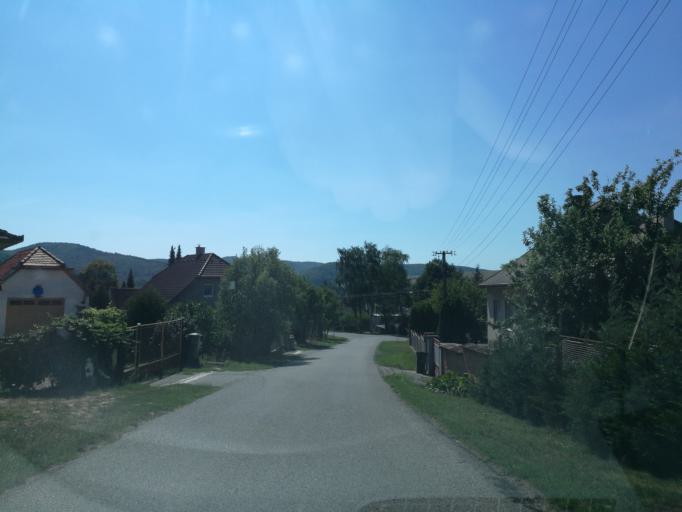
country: SK
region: Nitriansky
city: Brezova pod Bradlom
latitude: 48.6740
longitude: 17.5385
